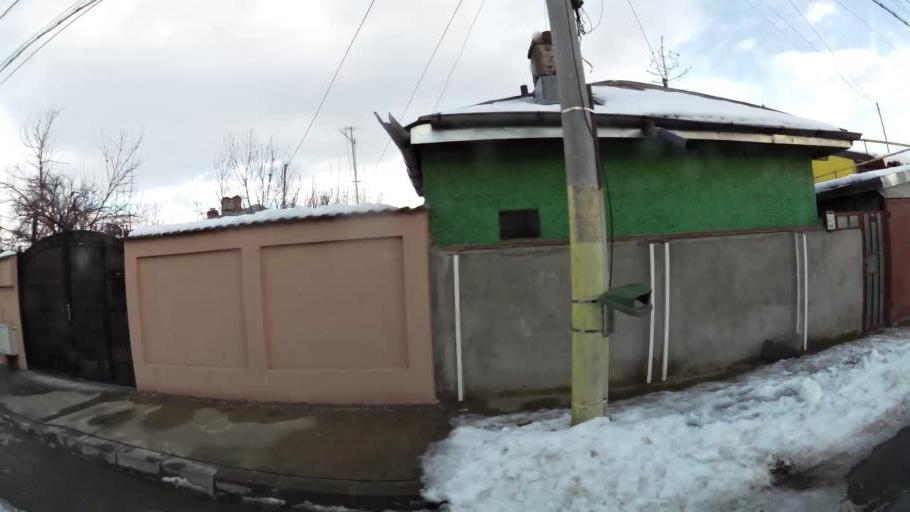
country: RO
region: Ilfov
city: Dobroesti
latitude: 44.4536
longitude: 26.1831
